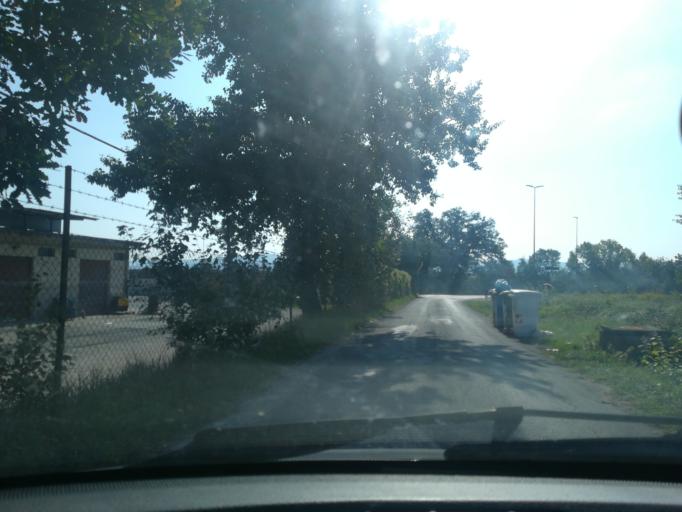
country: IT
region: The Marches
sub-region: Provincia di Macerata
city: Piediripa
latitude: 43.2721
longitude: 13.4686
